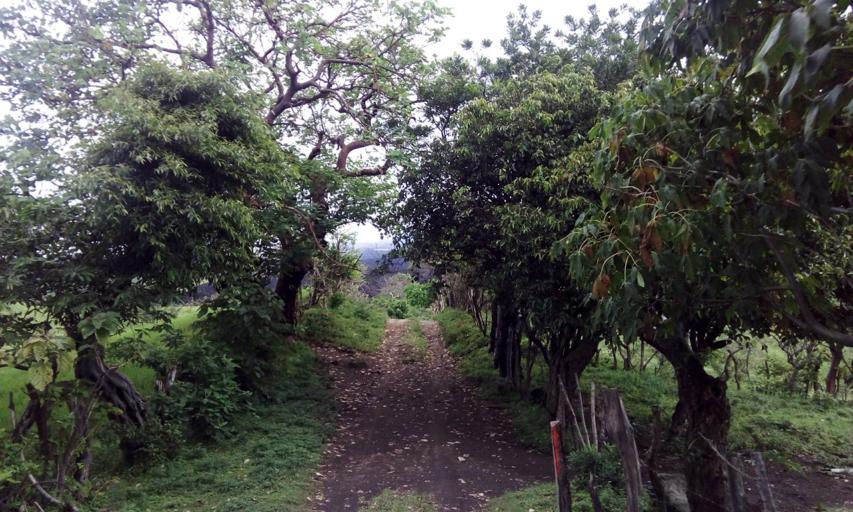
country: GT
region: Escuintla
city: San Vicente Pacaya
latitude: 14.3396
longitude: -90.6155
